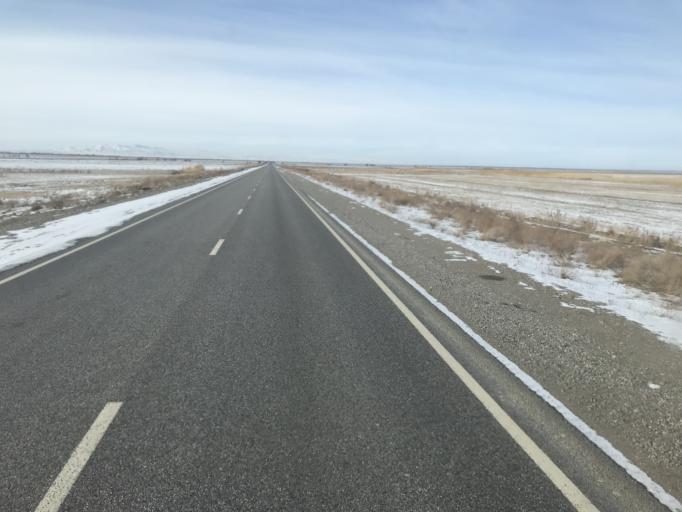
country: KZ
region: Zhambyl
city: Taraz
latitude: 43.0271
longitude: 71.3636
